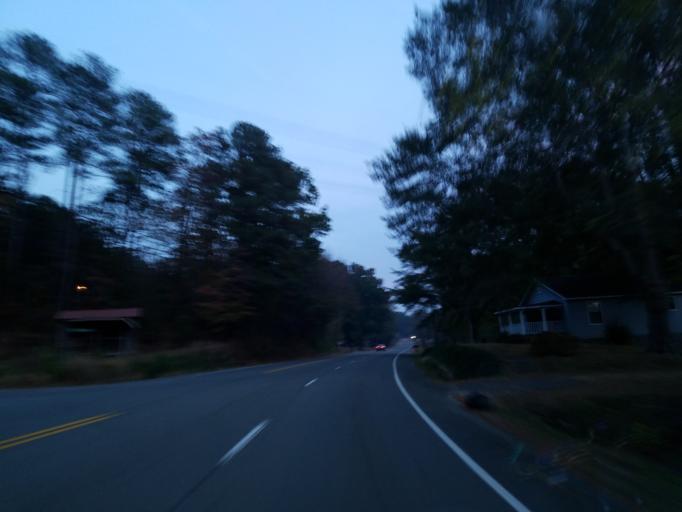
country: US
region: Georgia
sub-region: Pickens County
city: Jasper
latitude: 34.4990
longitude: -84.4732
